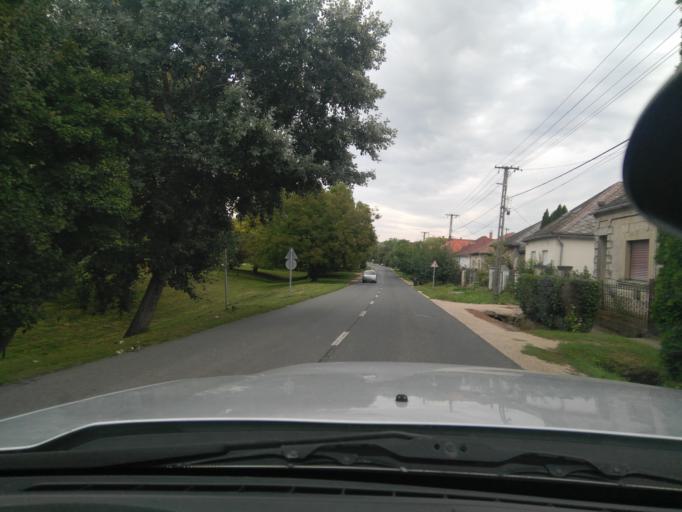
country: HU
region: Fejer
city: Val
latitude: 47.3662
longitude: 18.7366
